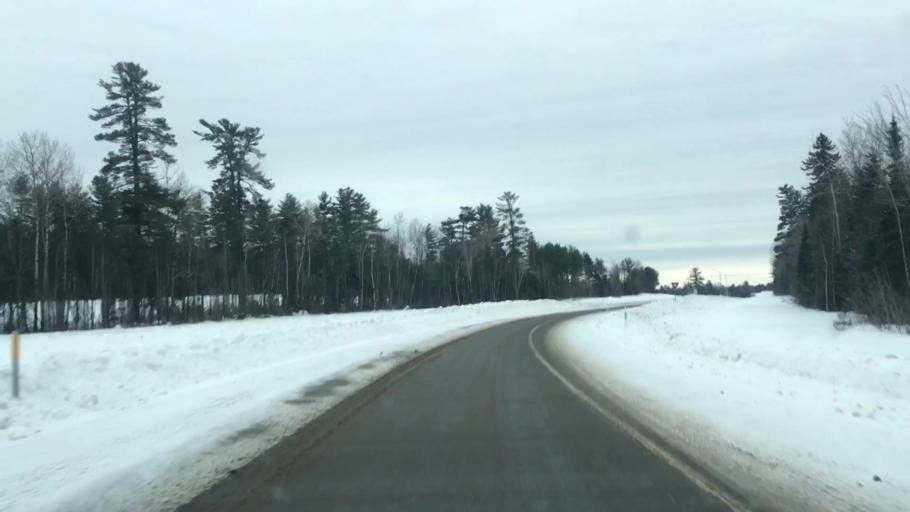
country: US
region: Maine
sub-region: Penobscot County
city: Lincoln
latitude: 45.3735
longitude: -68.6061
